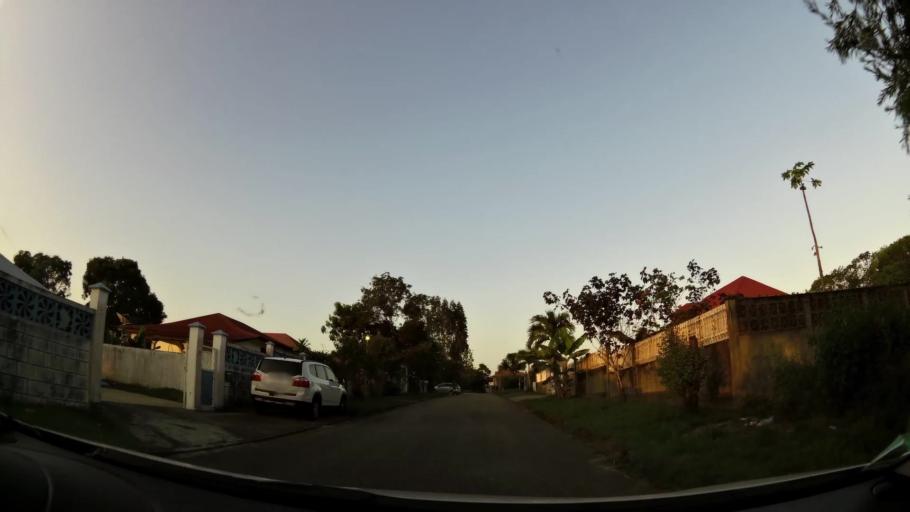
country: GF
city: Macouria
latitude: 4.9294
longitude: -52.4036
